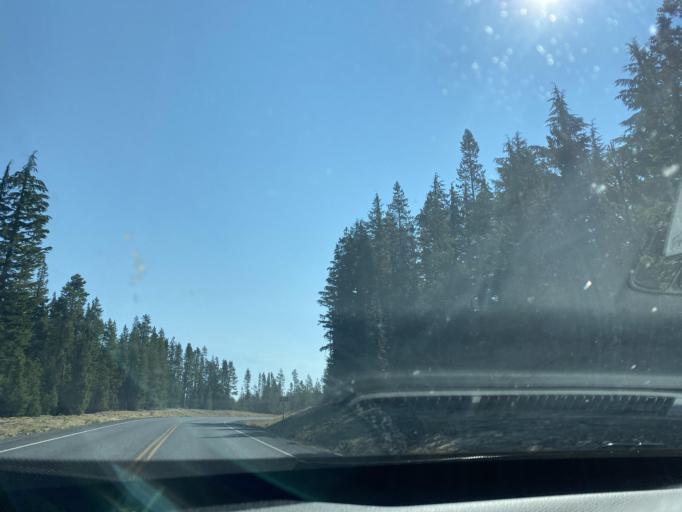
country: US
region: Oregon
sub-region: Deschutes County
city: Three Rivers
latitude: 43.7121
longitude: -121.2801
